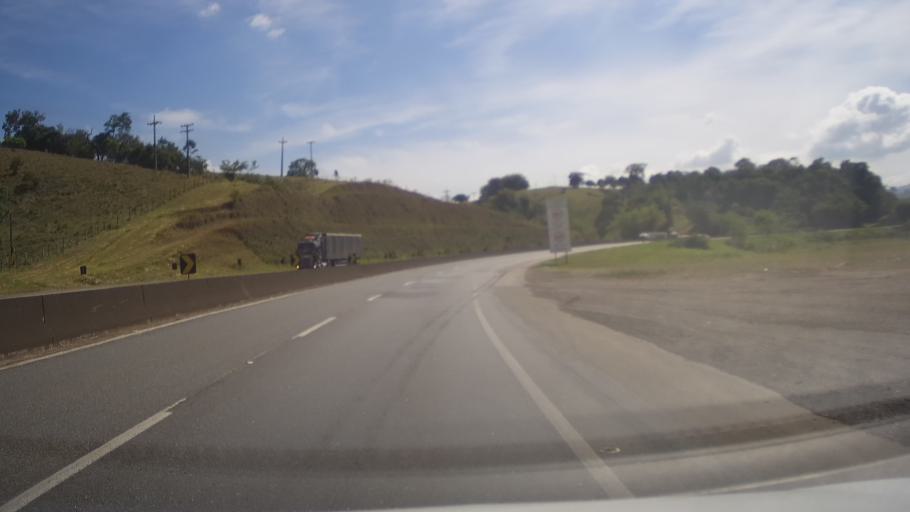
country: BR
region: Minas Gerais
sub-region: Cambui
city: Cambui
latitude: -22.5345
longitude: -46.0346
